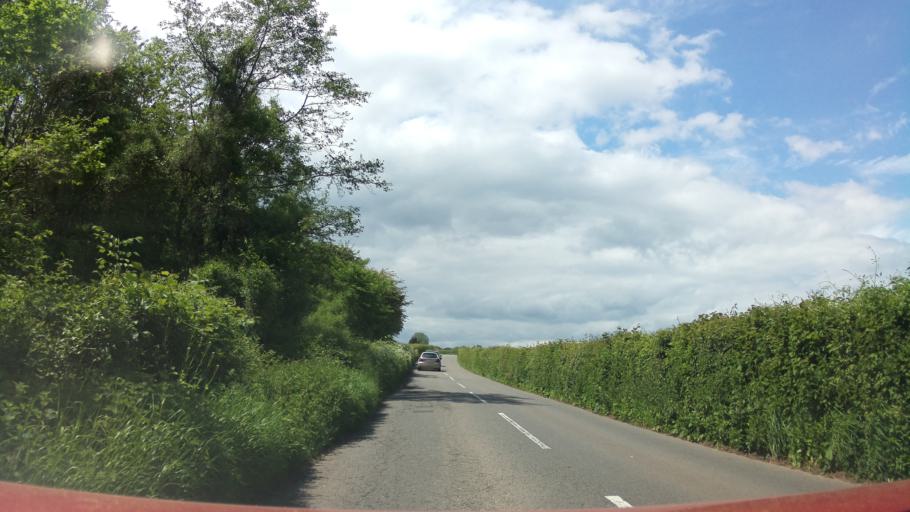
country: GB
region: England
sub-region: Herefordshire
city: Llanrothal
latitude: 51.8463
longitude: -2.7854
